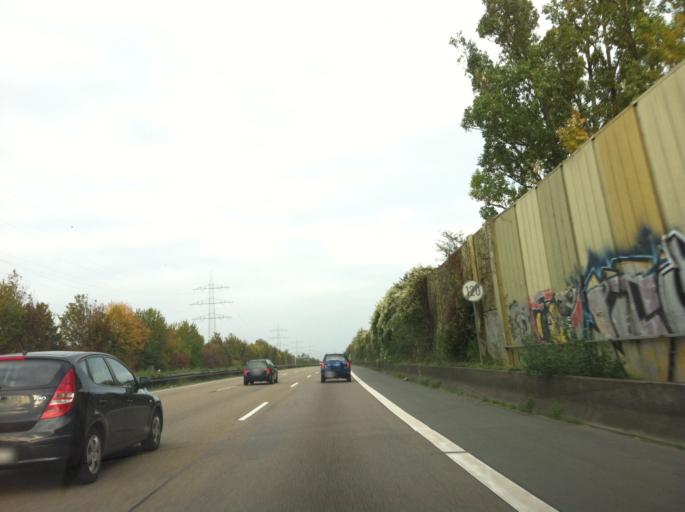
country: DE
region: Hesse
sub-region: Regierungsbezirk Darmstadt
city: Hattersheim
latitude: 50.0892
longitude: 8.4849
